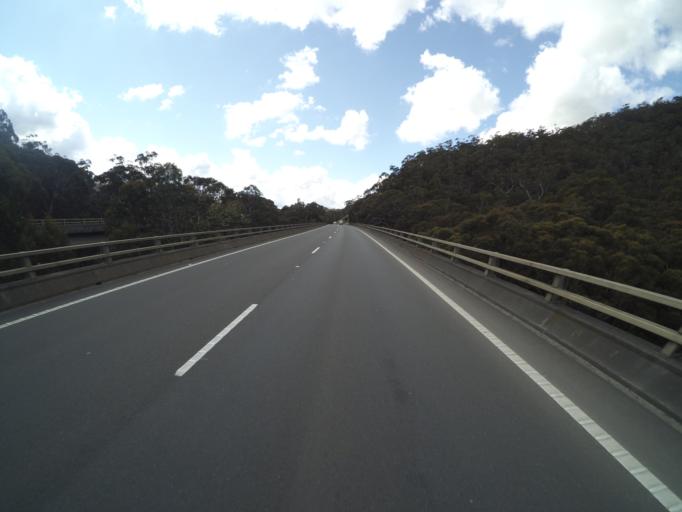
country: AU
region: New South Wales
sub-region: Wingecarribee
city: Mittagong
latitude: -34.4317
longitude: 150.4587
